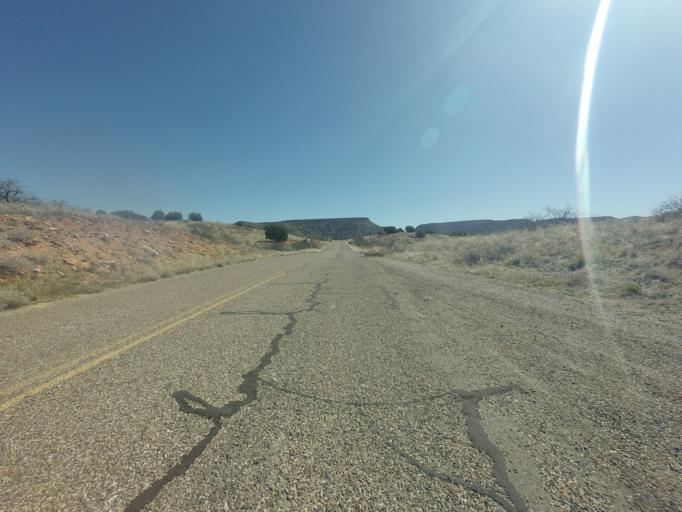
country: US
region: Arizona
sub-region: Yavapai County
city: Lake Montezuma
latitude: 34.6830
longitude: -111.7305
